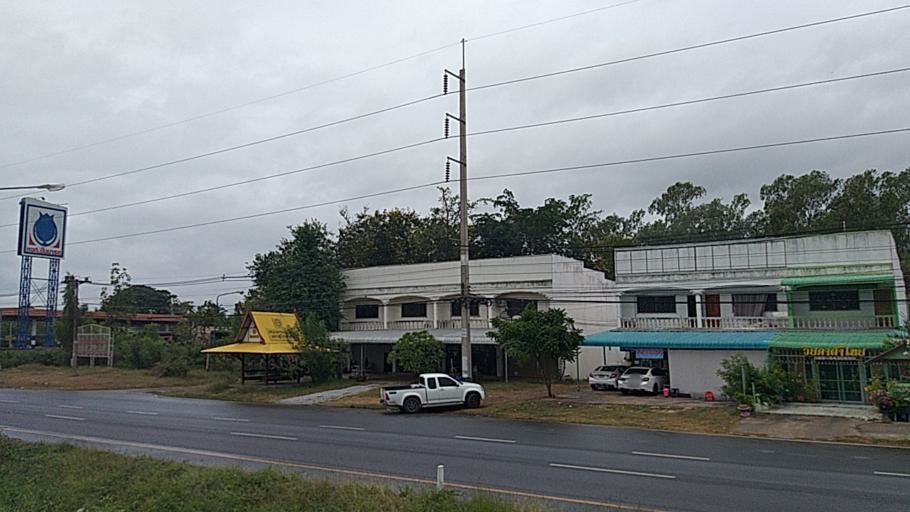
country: TH
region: Maha Sarakham
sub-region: Amphoe Borabue
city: Borabue
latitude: 16.0529
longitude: 103.1308
